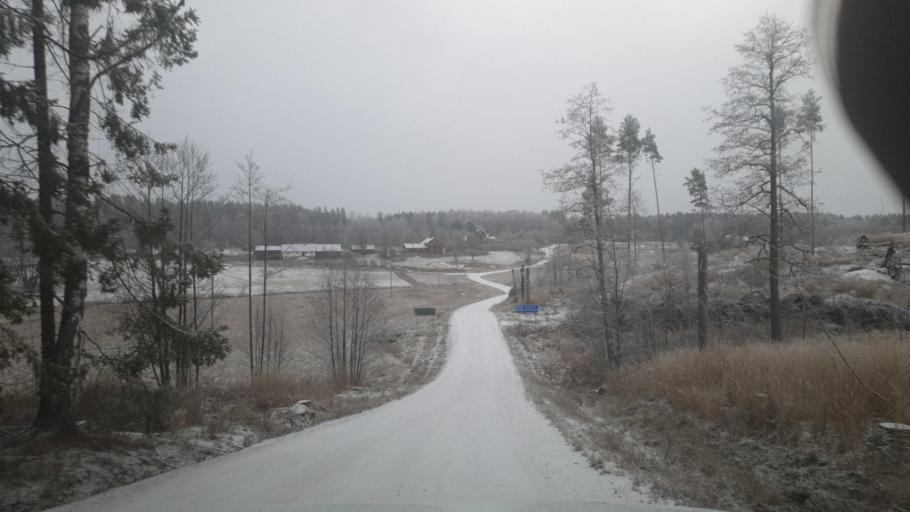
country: SE
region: Vaermland
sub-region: Grums Kommun
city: Grums
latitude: 59.5377
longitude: 12.8792
